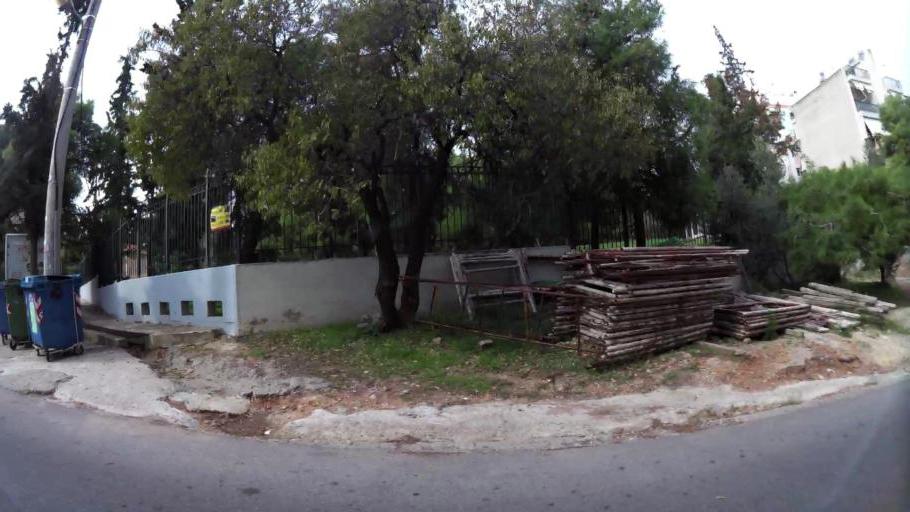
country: GR
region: Attica
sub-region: Nomarchia Athinas
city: Chaidari
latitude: 38.0211
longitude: 23.6711
